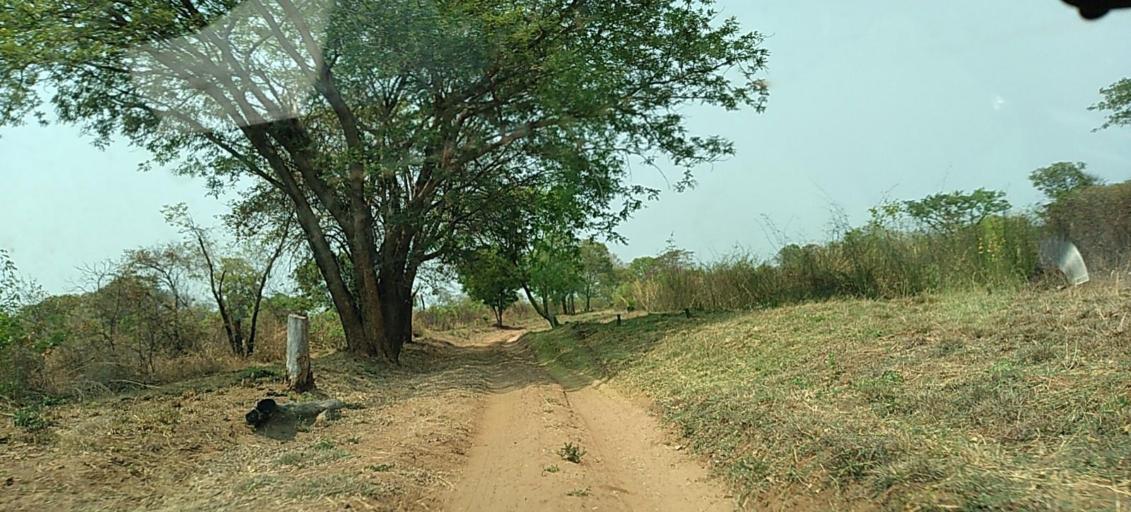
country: ZM
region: Western
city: Lukulu
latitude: -13.9717
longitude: 23.2303
